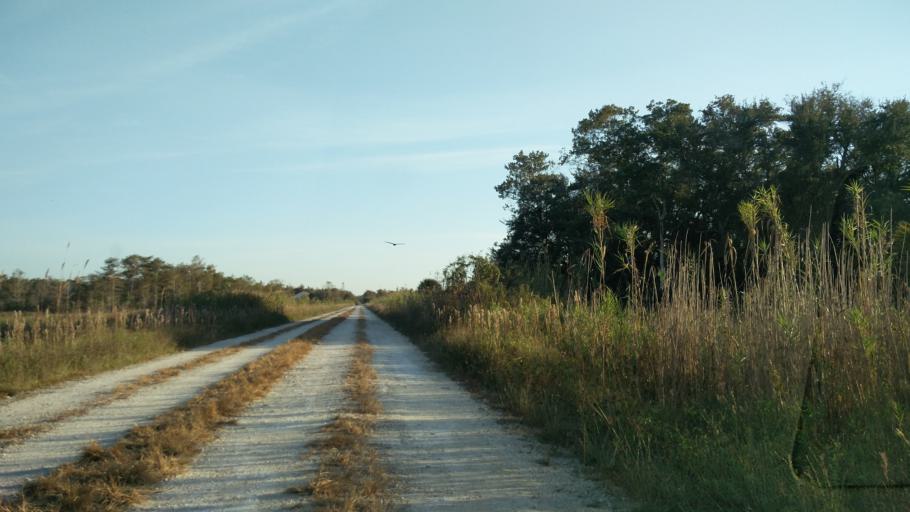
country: US
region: Florida
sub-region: Collier County
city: Lely Resort
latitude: 25.9610
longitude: -81.3642
